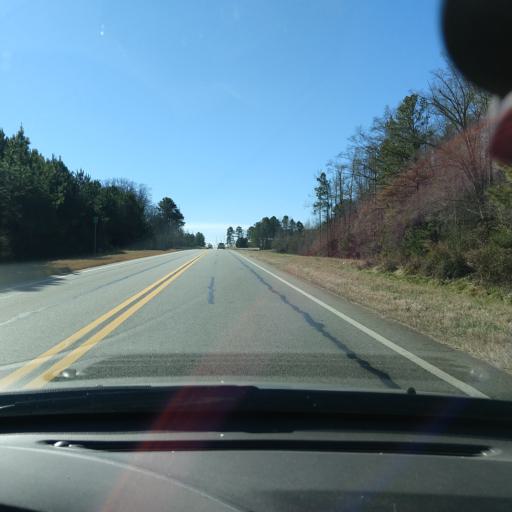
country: US
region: Georgia
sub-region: Walton County
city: Social Circle
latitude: 33.6573
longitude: -83.6893
